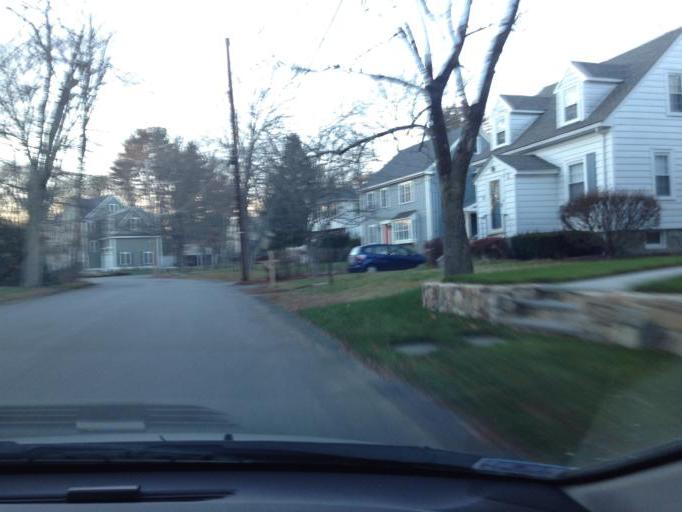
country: US
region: Massachusetts
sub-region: Middlesex County
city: Bedford
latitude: 42.4956
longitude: -71.2774
